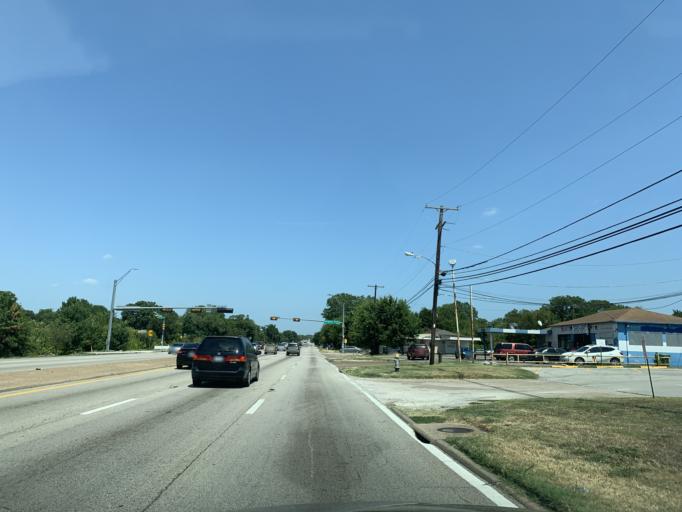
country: US
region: Texas
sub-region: Dallas County
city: Hutchins
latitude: 32.6824
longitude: -96.8038
